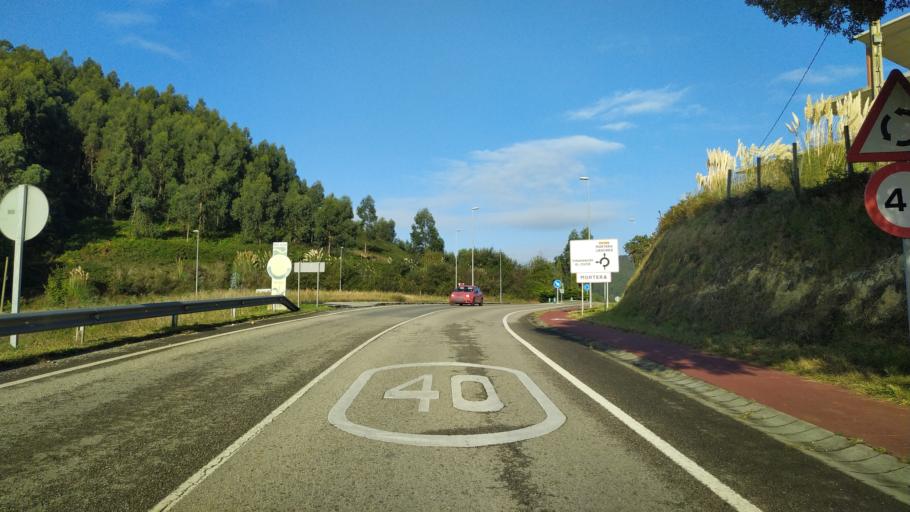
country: ES
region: Cantabria
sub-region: Provincia de Cantabria
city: Santa Cruz de Bezana
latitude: 43.4398
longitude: -3.9223
